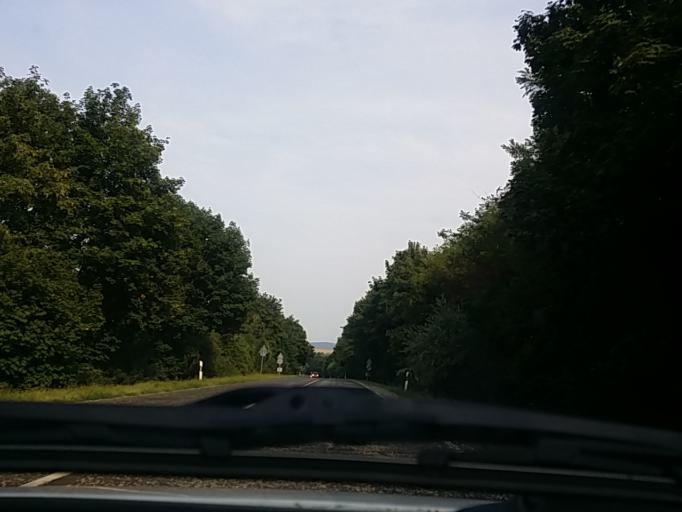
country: HU
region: Fejer
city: Etyek
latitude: 47.4946
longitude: 18.7355
